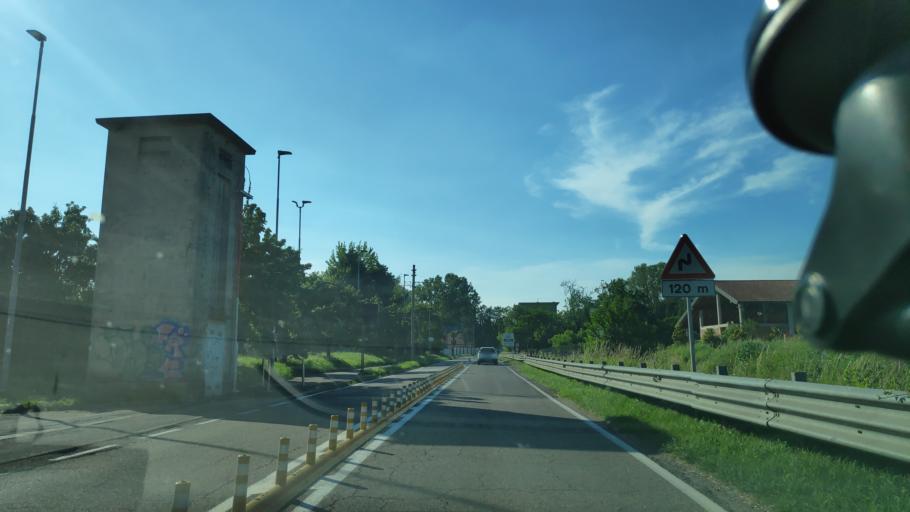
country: IT
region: Lombardy
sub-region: Citta metropolitana di Milano
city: Basiglio
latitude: 45.3689
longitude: 9.1502
